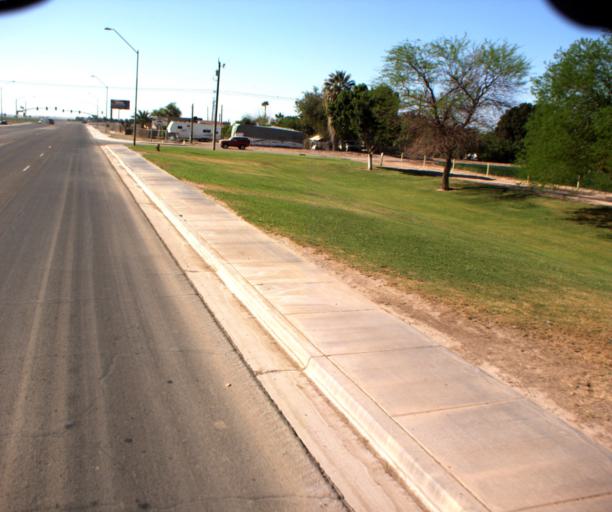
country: US
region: Arizona
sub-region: Yuma County
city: San Luis
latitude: 32.5551
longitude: -114.7849
